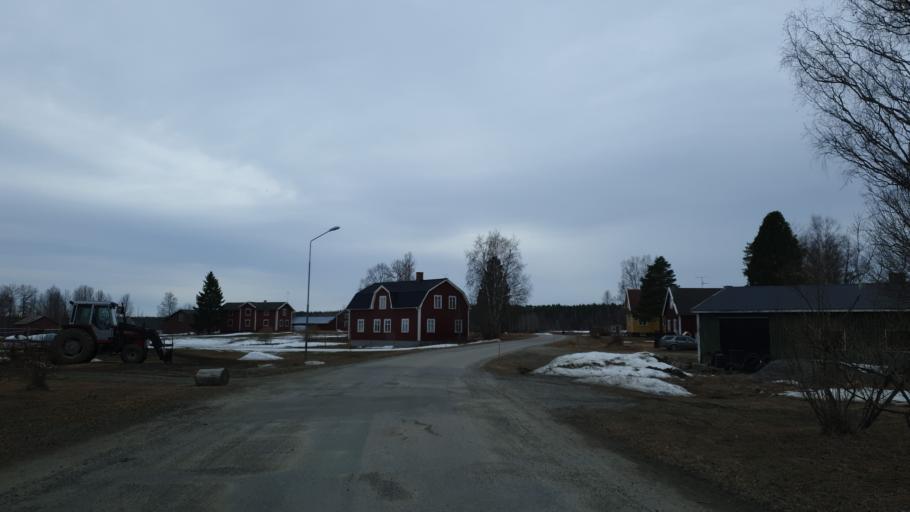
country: SE
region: Vaesterbotten
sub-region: Robertsfors Kommun
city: Robertsfors
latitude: 64.4027
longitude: 21.0083
